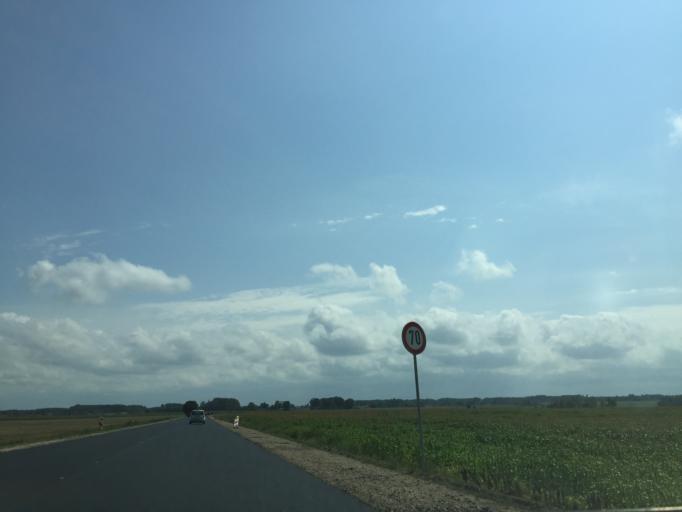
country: LV
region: Vilanu
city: Vilani
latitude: 56.6019
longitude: 26.8606
